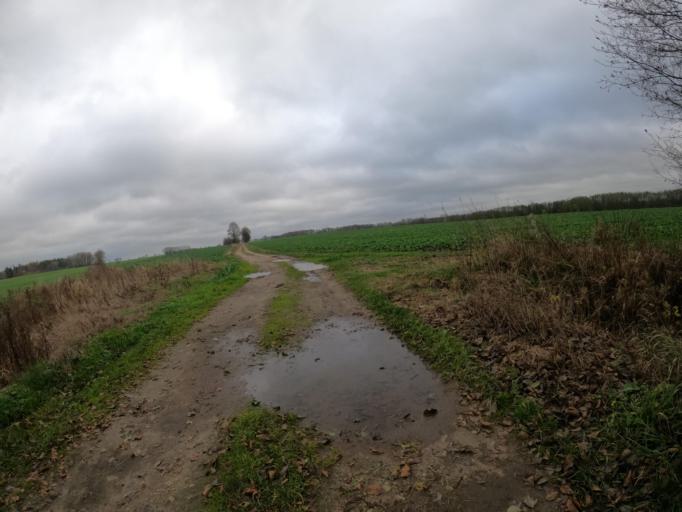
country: PL
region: West Pomeranian Voivodeship
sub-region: Powiat walecki
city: Tuczno
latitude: 53.2750
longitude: 16.1652
